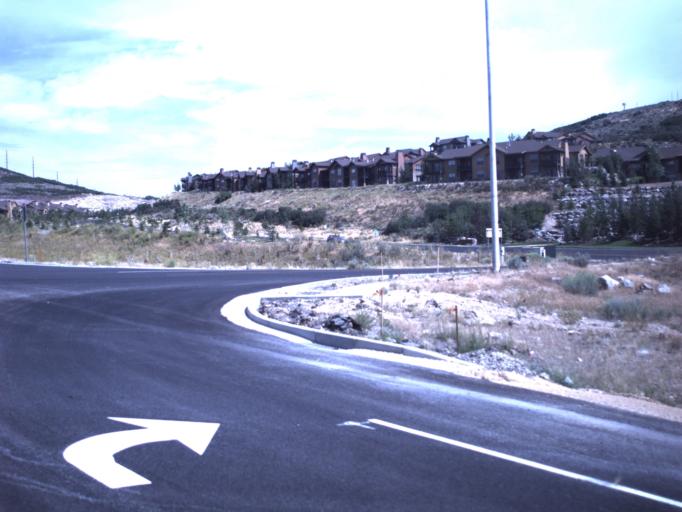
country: US
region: Utah
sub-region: Summit County
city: Park City
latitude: 40.6772
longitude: -111.4316
